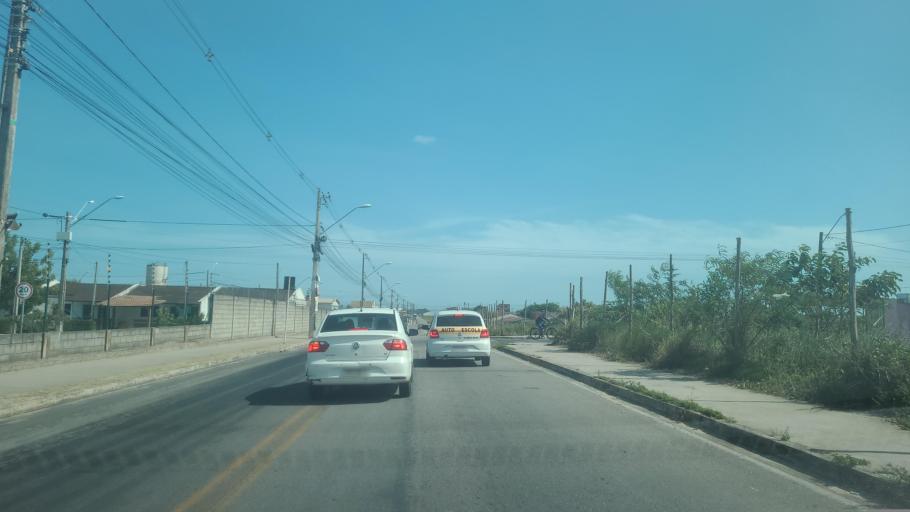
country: BR
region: Alagoas
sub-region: Satuba
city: Satuba
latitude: -9.5292
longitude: -35.7760
